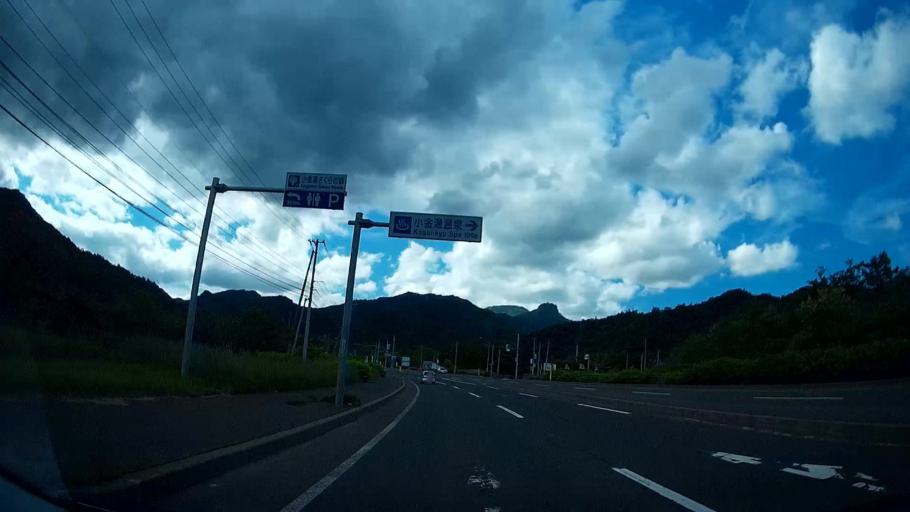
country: JP
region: Hokkaido
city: Sapporo
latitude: 42.9646
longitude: 141.2208
